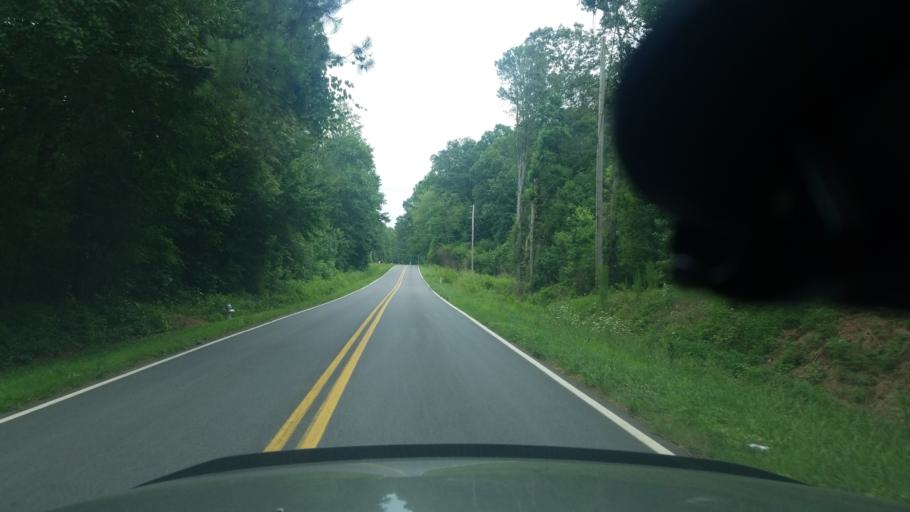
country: US
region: Georgia
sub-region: Dawson County
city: Dawsonville
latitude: 34.3283
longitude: -84.1791
